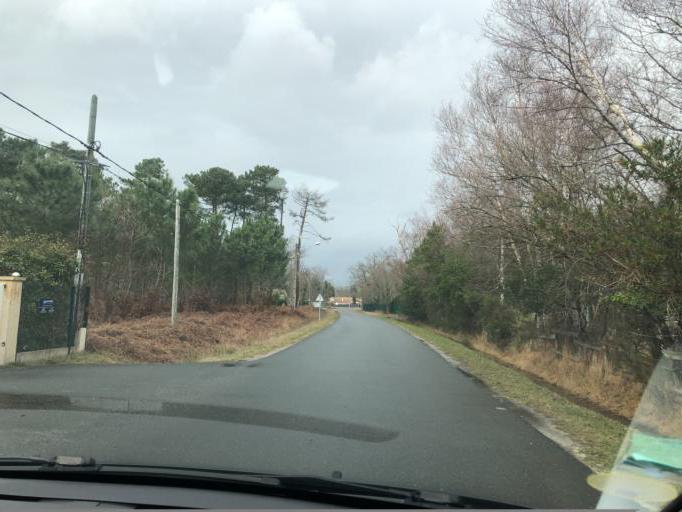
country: FR
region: Aquitaine
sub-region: Departement de la Gironde
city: Hourtin
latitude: 45.1795
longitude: -1.0750
